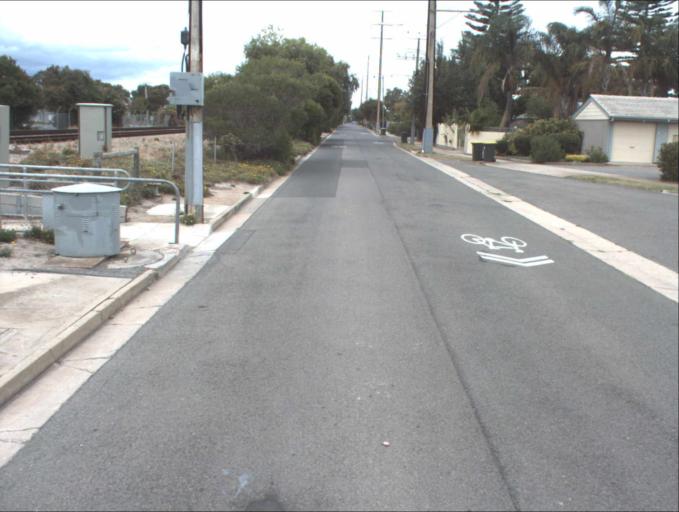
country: AU
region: South Australia
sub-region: Port Adelaide Enfield
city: Birkenhead
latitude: -34.8002
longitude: 138.4989
